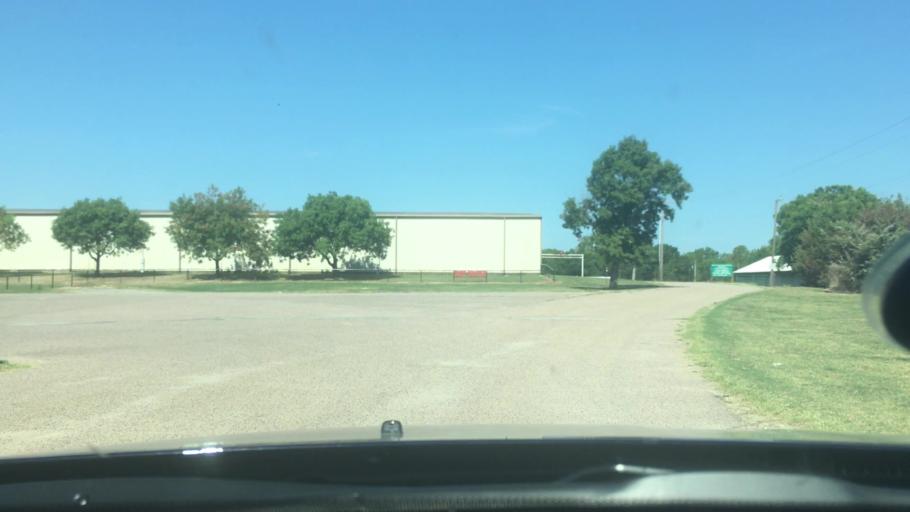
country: US
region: Oklahoma
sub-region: Bryan County
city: Durant
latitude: 33.9762
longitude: -96.3910
